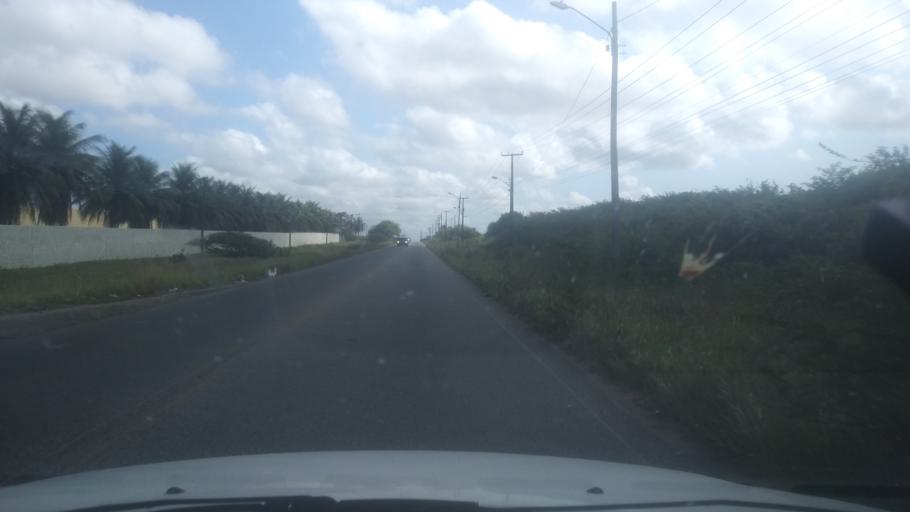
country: BR
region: Rio Grande do Norte
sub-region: Extremoz
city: Extremoz
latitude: -5.7178
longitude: -35.2774
